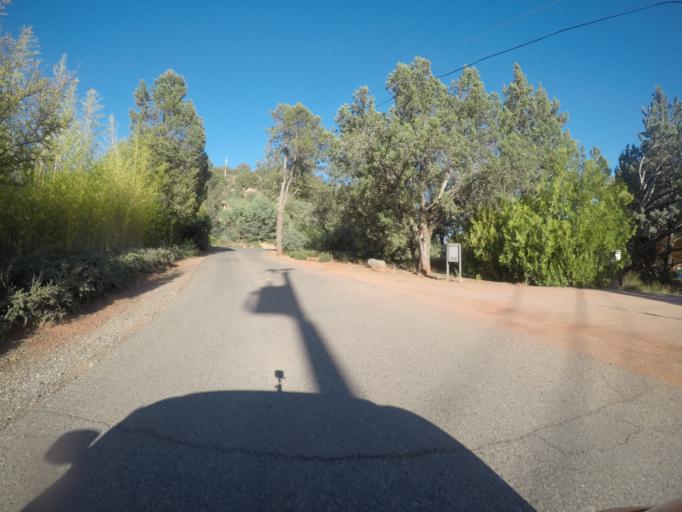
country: US
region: Arizona
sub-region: Yavapai County
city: West Sedona
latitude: 34.8292
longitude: -111.7941
